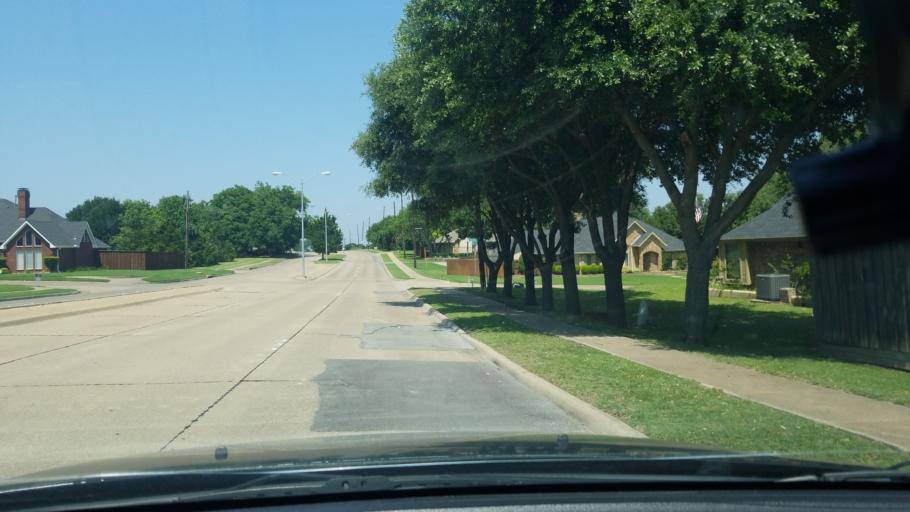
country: US
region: Texas
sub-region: Dallas County
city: Mesquite
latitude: 32.8246
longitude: -96.6156
